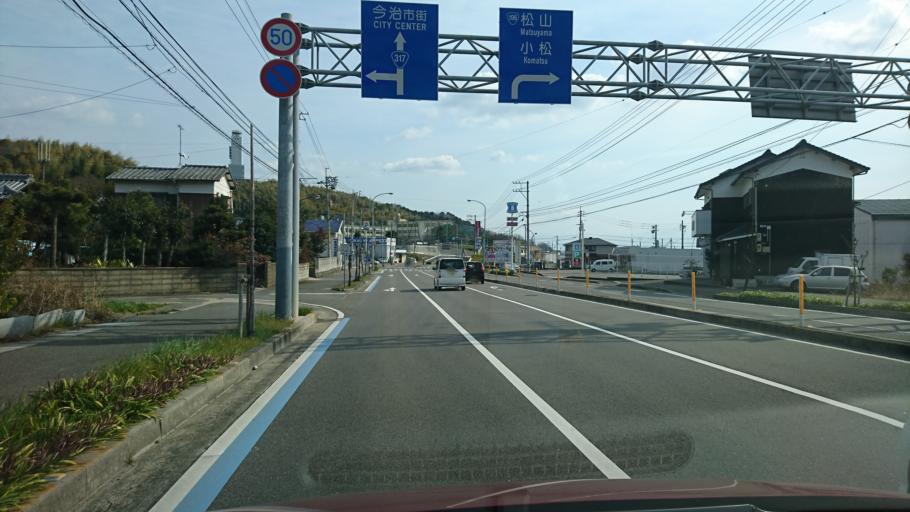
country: JP
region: Ehime
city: Hojo
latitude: 34.0905
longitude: 132.9823
